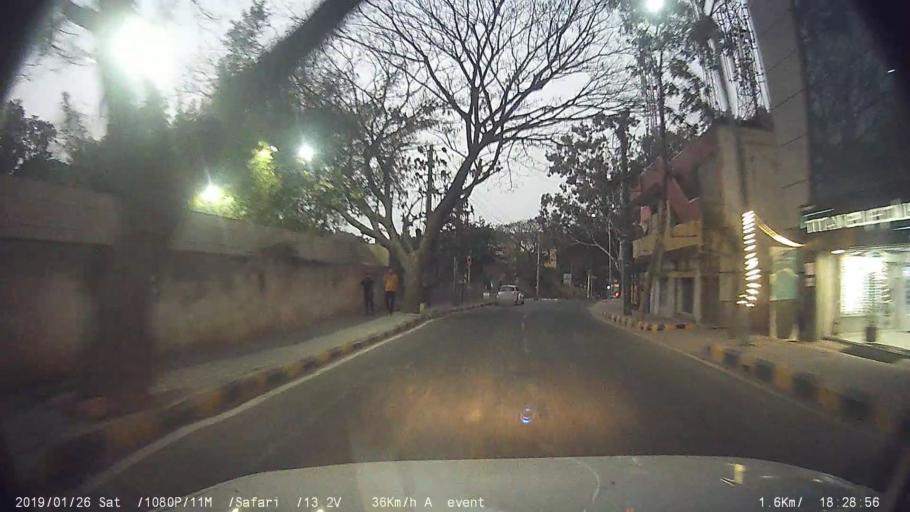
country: IN
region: Karnataka
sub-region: Bangalore Urban
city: Anekal
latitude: 12.8476
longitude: 77.6622
